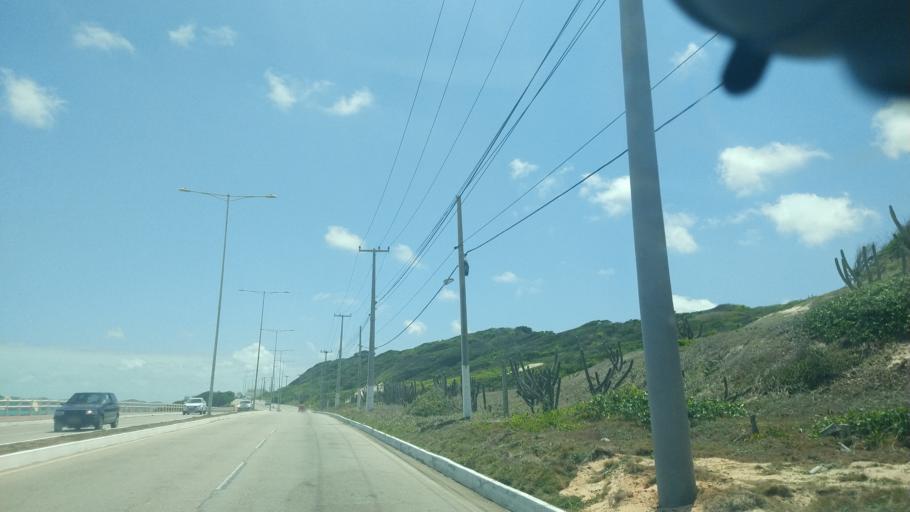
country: BR
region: Rio Grande do Norte
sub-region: Natal
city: Natal
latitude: -5.8359
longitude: -35.1826
